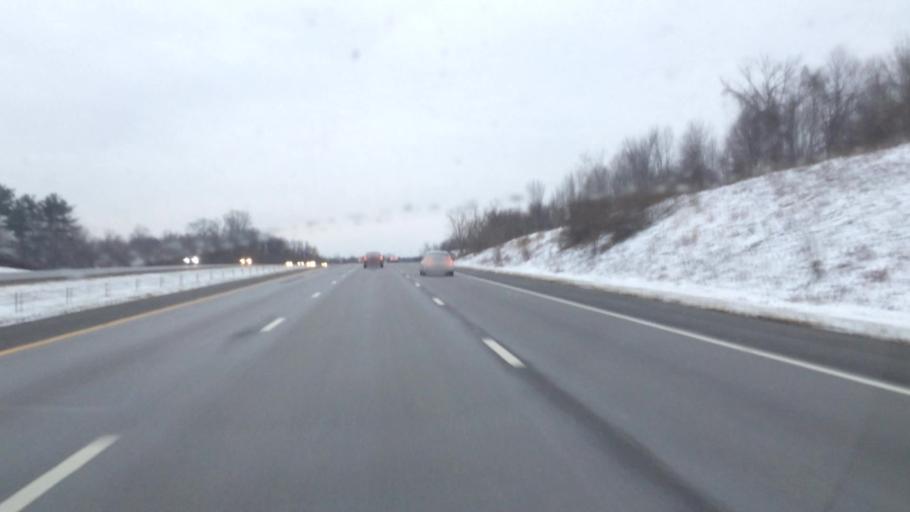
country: US
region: Ohio
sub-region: Medina County
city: Medina
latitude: 41.1735
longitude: -81.7868
